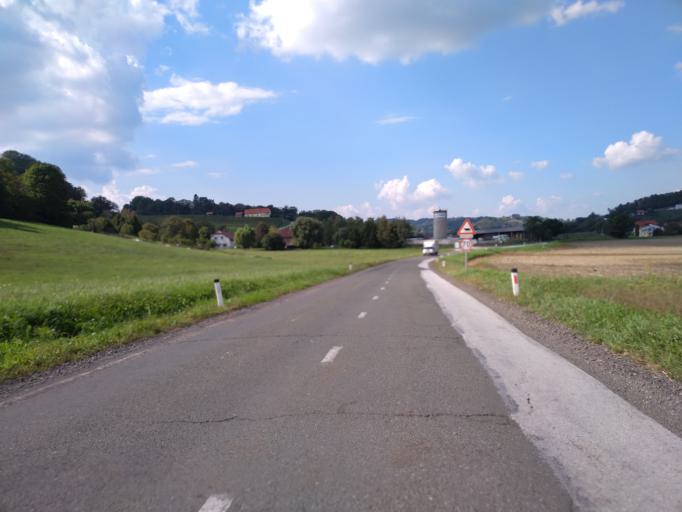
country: SI
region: Pesnica
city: Pesnica pri Mariboru
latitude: 46.5980
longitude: 15.6582
